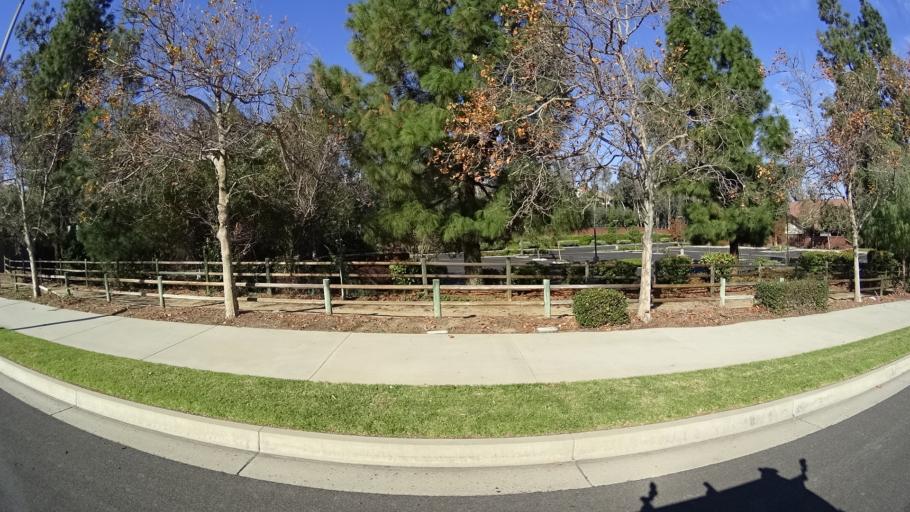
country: US
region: California
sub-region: Orange County
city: North Tustin
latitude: 33.7825
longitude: -117.7725
